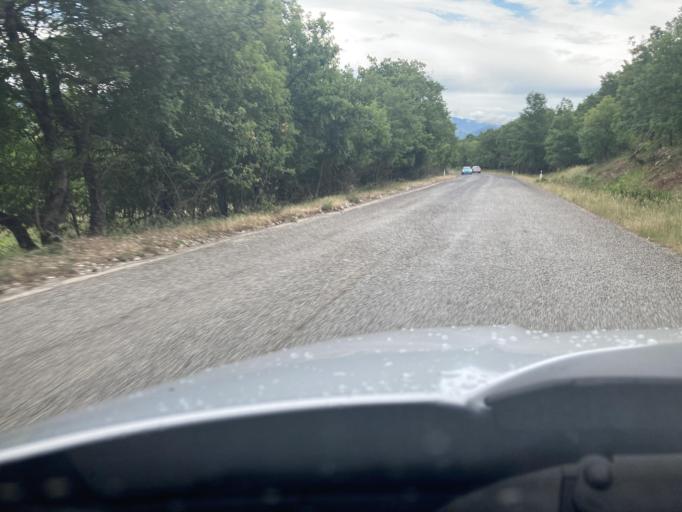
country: IT
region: Abruzzo
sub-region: Provincia dell' Aquila
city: San Panfilo d'Ocre
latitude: 42.2798
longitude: 13.4643
